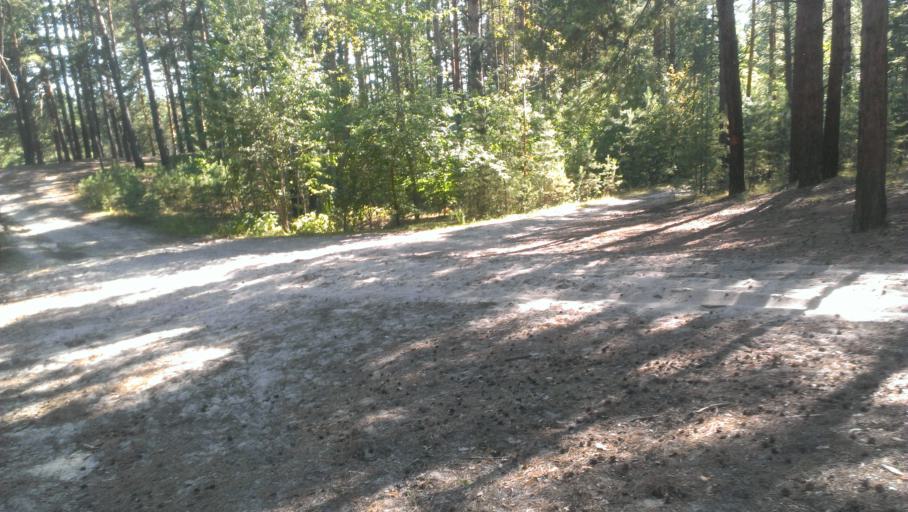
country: RU
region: Altai Krai
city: Yuzhnyy
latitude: 53.3160
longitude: 83.6889
